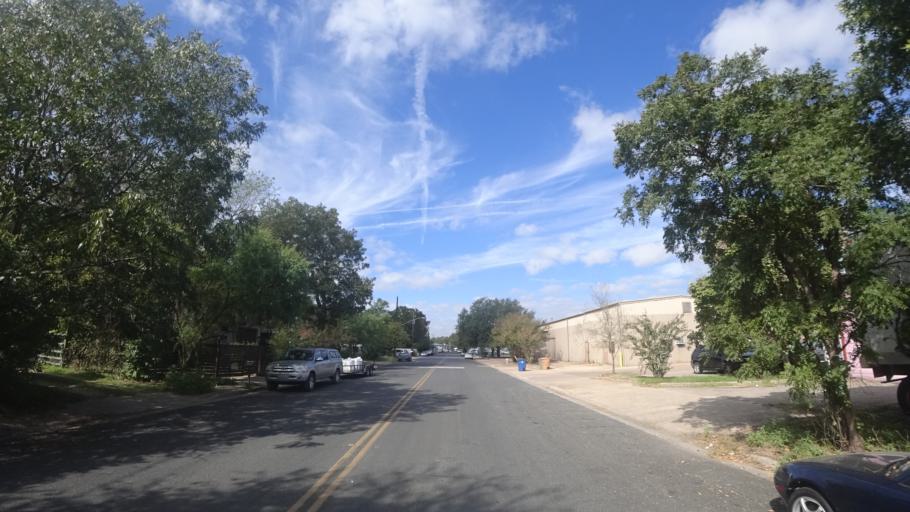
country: US
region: Texas
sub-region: Travis County
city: Austin
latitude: 30.2507
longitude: -97.7006
